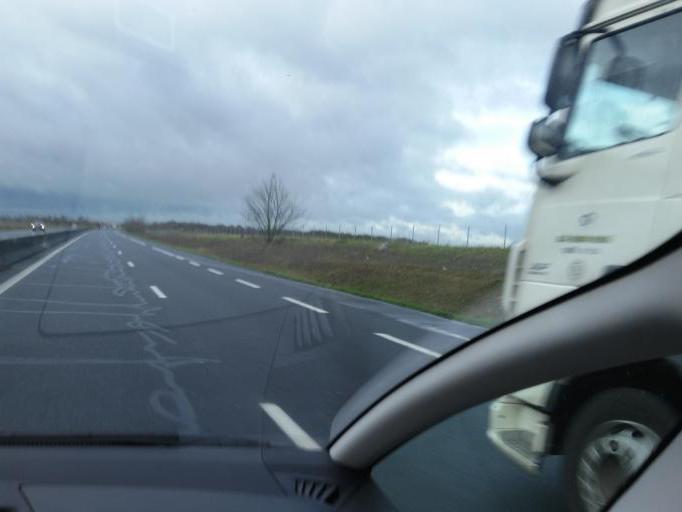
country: FR
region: Picardie
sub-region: Departement de la Somme
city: Boves
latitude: 49.8569
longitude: 2.4440
